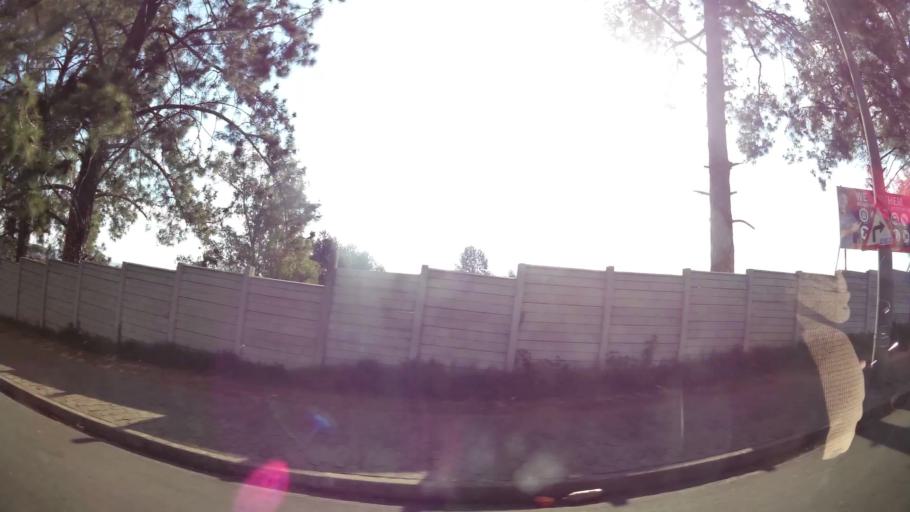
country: ZA
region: Gauteng
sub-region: West Rand District Municipality
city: Krugersdorp
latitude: -26.0952
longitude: 27.7764
